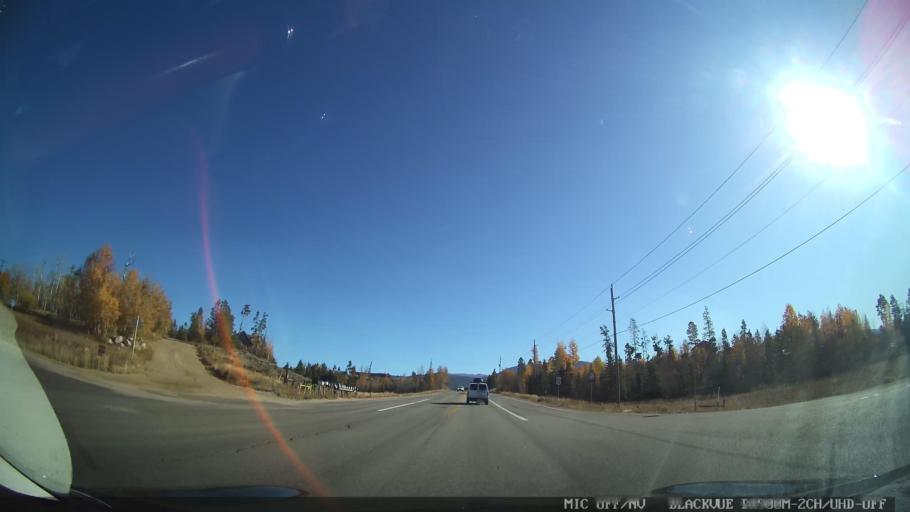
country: US
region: Colorado
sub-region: Grand County
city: Granby
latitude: 40.1957
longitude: -105.8750
